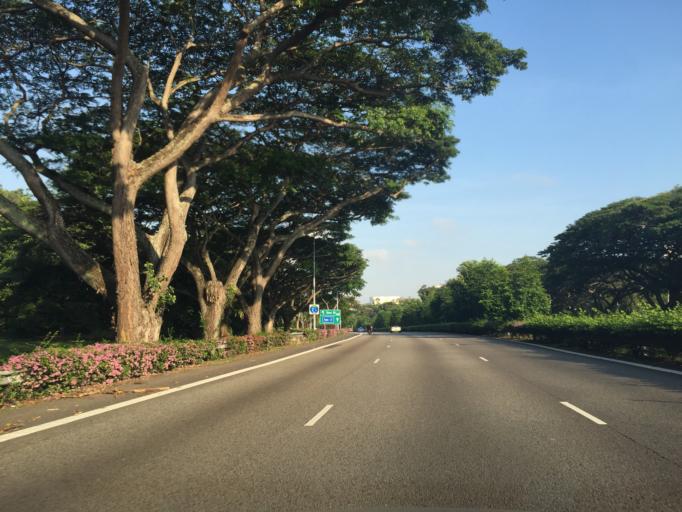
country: SG
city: Singapore
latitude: 1.3499
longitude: 103.9636
